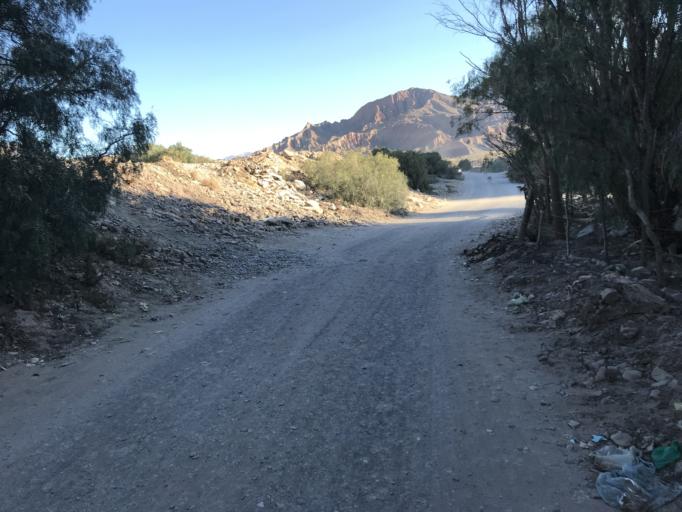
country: AR
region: Jujuy
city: Maimara
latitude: -23.5791
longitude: -65.4017
